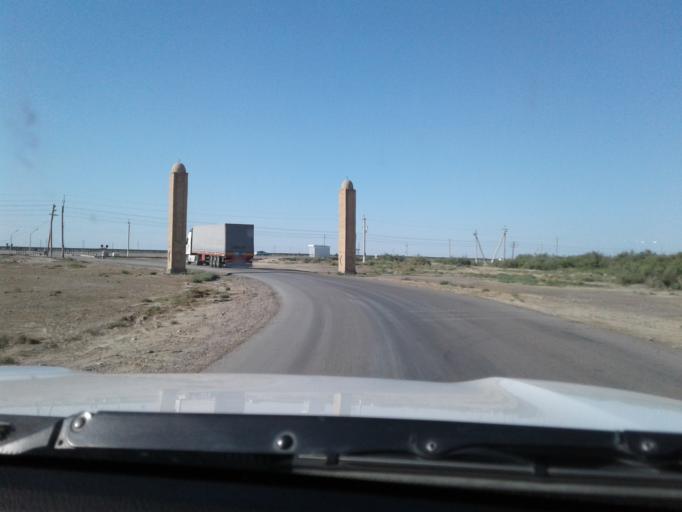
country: IR
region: Razavi Khorasan
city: Kalat-e Naderi
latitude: 37.2017
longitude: 60.0423
